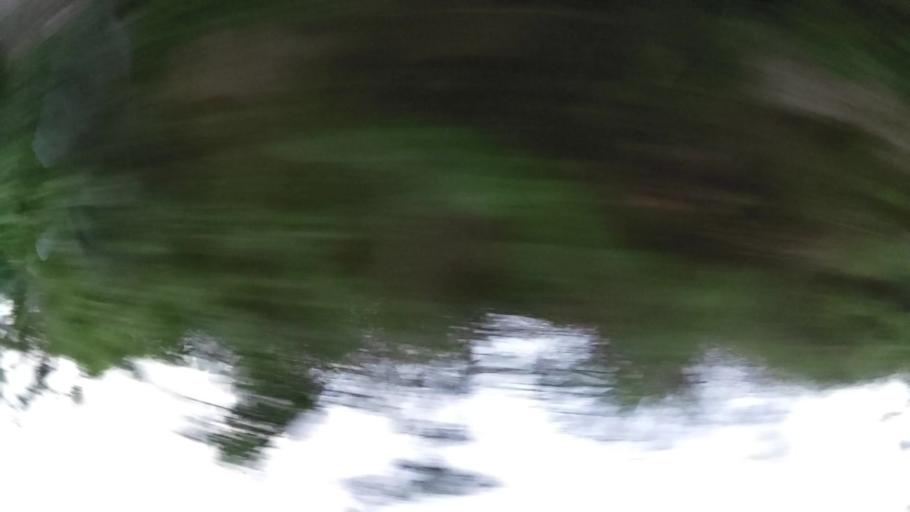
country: BB
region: Saint Philip
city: Crane
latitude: 13.1183
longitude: -59.4935
